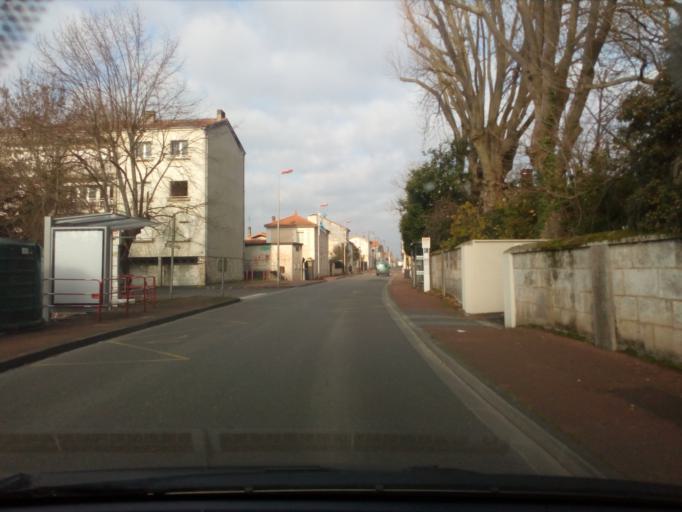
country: FR
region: Poitou-Charentes
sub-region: Departement de la Charente
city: Gond-Pontouvre
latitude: 45.6730
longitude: 0.1593
